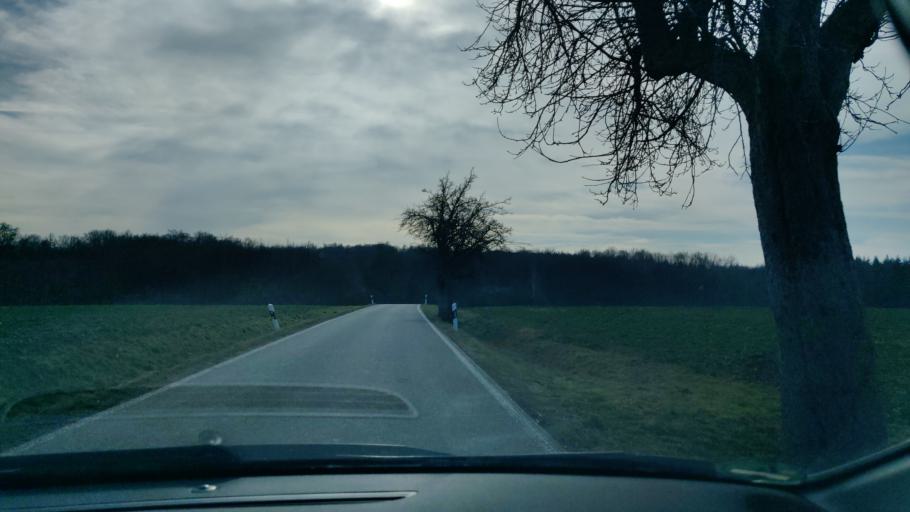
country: DE
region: Saxony
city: Rochlitz
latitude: 51.0378
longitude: 12.7816
